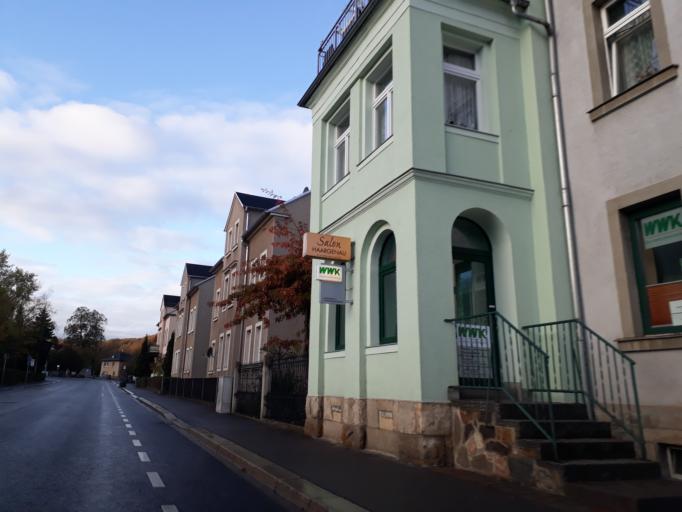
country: DE
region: Saxony
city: Rabenau
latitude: 50.9821
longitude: 13.6315
